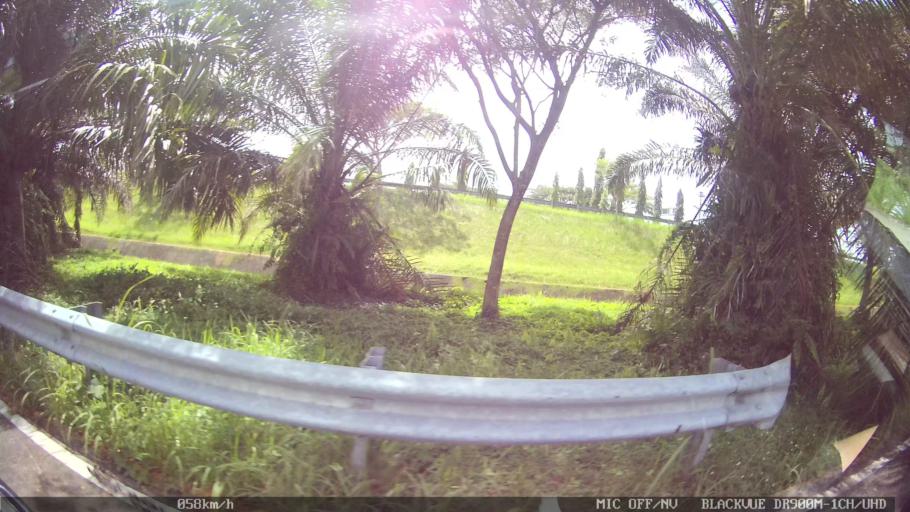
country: ID
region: North Sumatra
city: Percut
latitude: 3.6349
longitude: 98.8752
